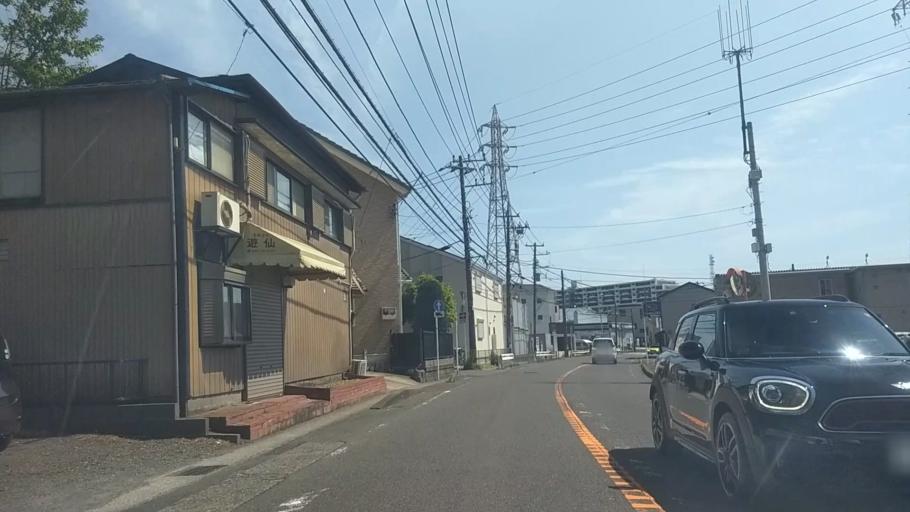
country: JP
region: Kanagawa
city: Kamakura
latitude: 35.3568
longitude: 139.5454
